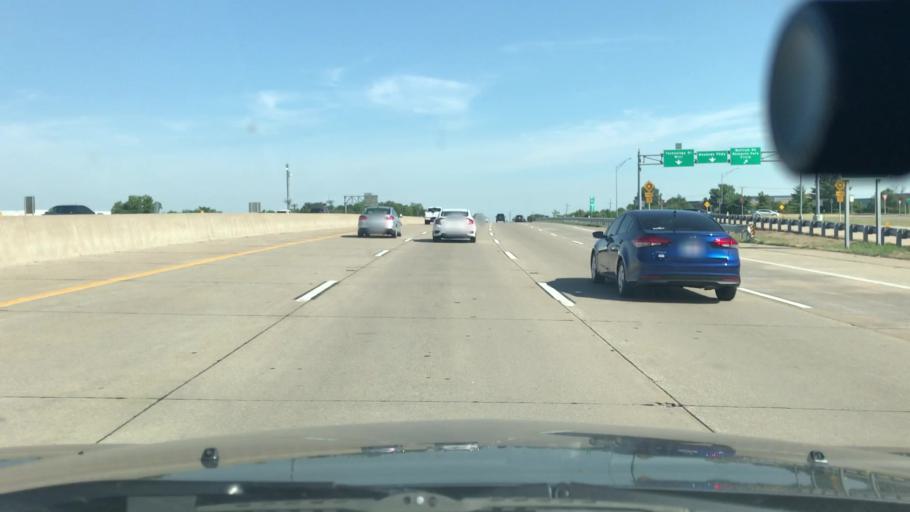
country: US
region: Missouri
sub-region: Saint Charles County
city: Weldon Spring
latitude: 38.7036
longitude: -90.6736
